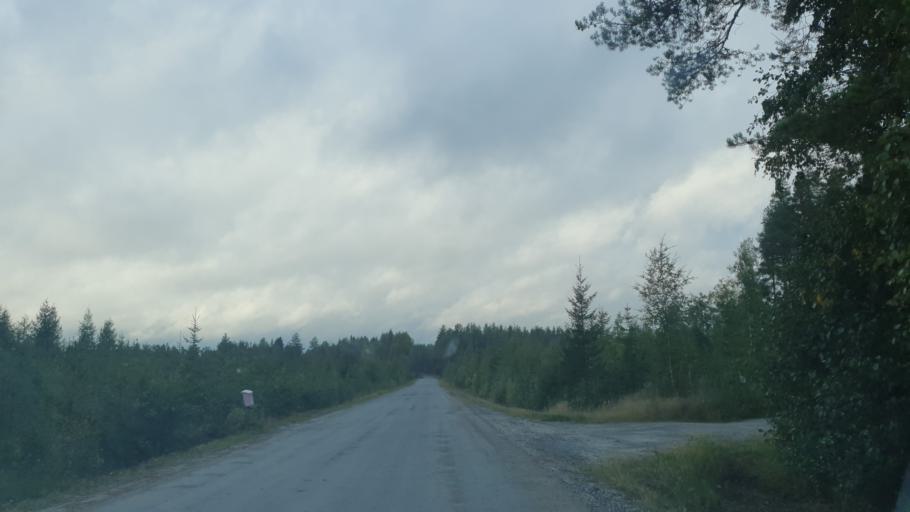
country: FI
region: Kainuu
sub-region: Kehys-Kainuu
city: Kuhmo
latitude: 64.1341
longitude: 29.5780
